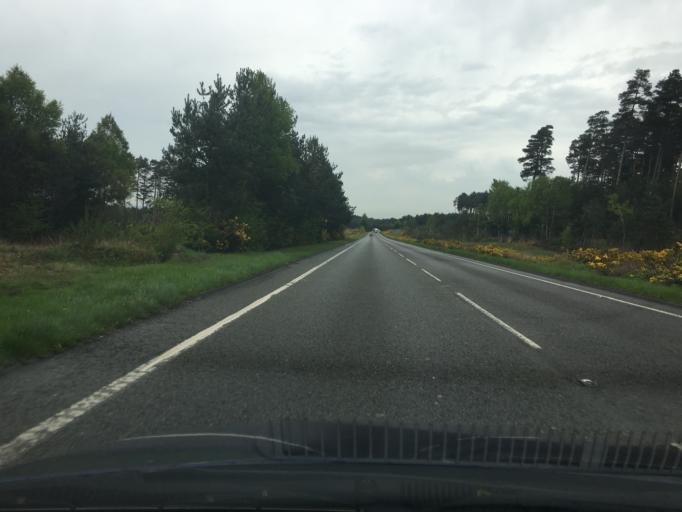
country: GB
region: England
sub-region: Bracknell Forest
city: Crowthorne
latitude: 51.3749
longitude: -0.7676
